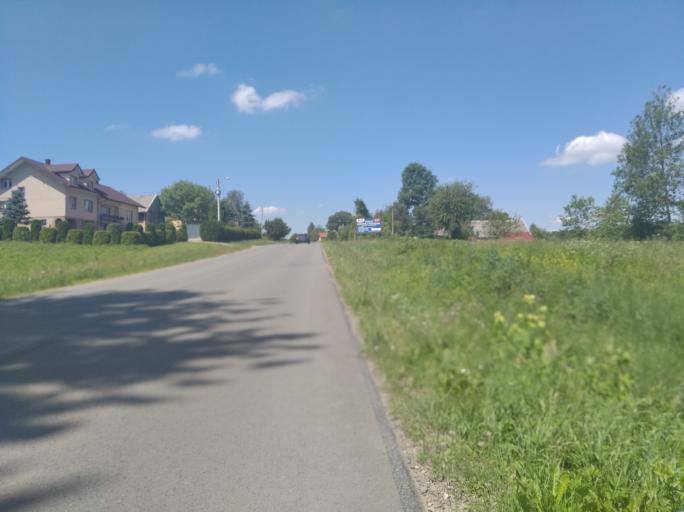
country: PL
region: Subcarpathian Voivodeship
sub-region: Powiat brzozowski
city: Jablonka
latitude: 49.6973
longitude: 22.1356
